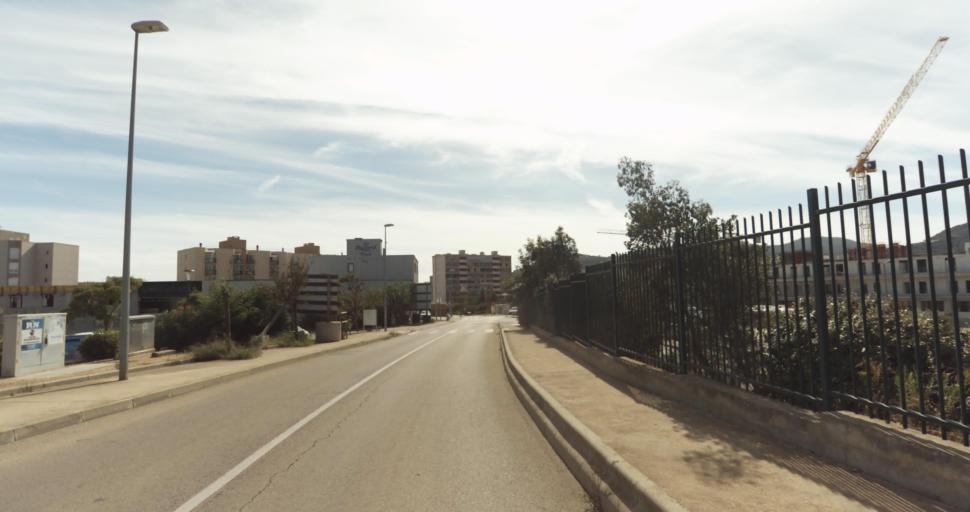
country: FR
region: Corsica
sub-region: Departement de la Corse-du-Sud
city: Ajaccio
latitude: 41.9423
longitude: 8.7469
